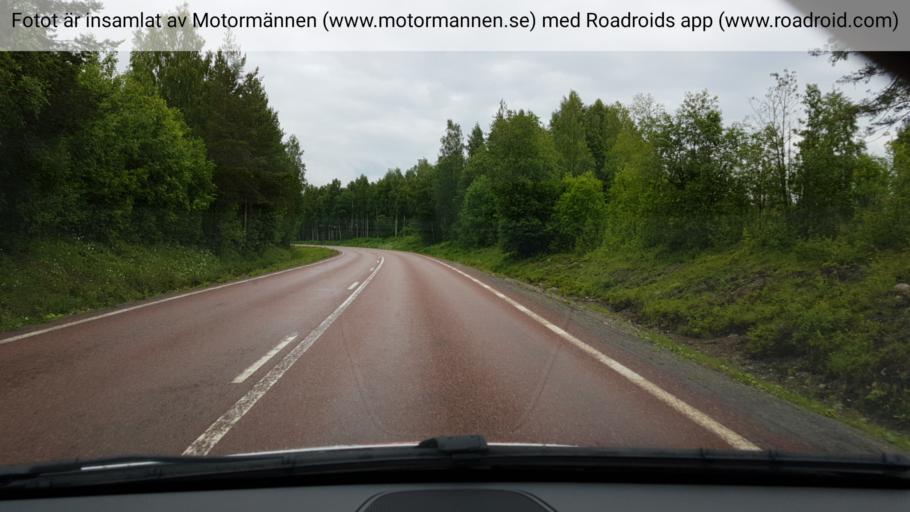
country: SE
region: Jaemtland
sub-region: Stroemsunds Kommun
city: Stroemsund
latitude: 63.9817
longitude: 15.8851
